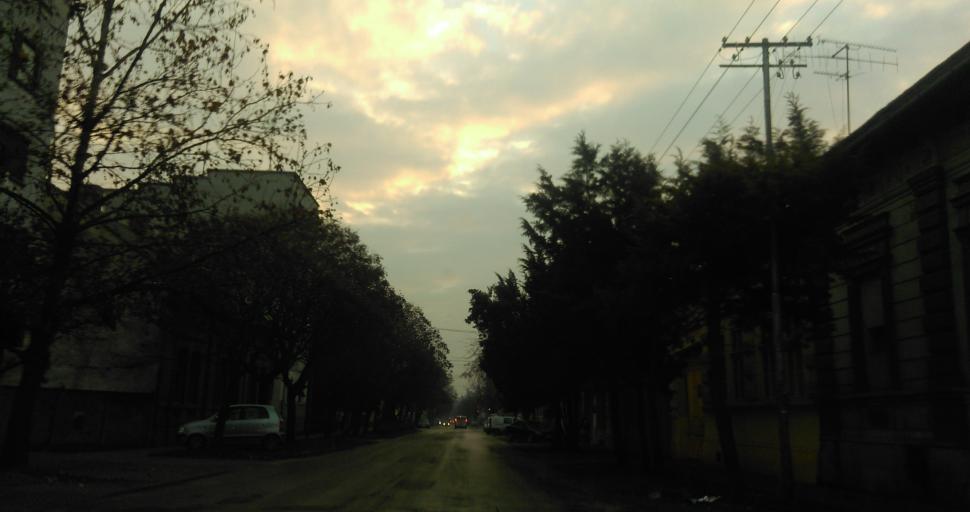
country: RS
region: Autonomna Pokrajina Vojvodina
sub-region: Juznobacki Okrug
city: Becej
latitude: 45.6188
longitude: 20.0432
